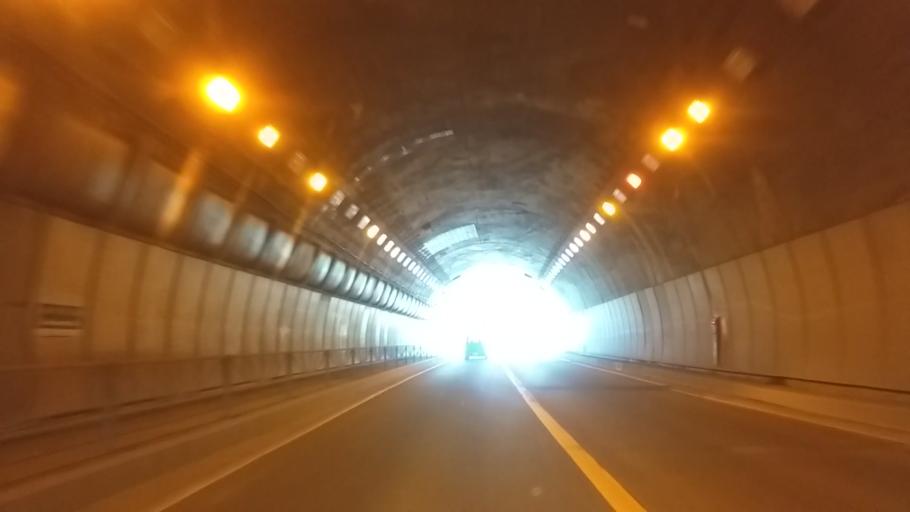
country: JP
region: Shizuoka
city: Fujinomiya
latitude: 35.2829
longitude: 138.4488
